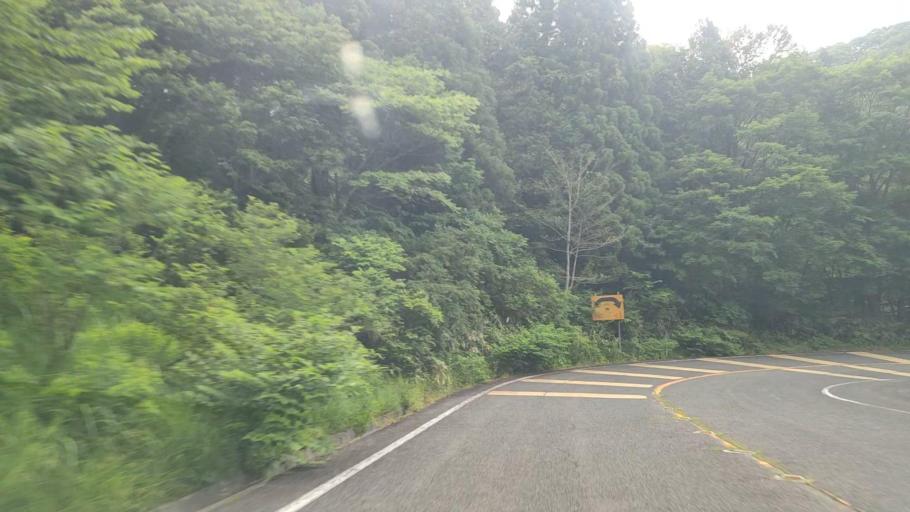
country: JP
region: Tottori
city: Yonago
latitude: 35.3260
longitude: 133.5673
